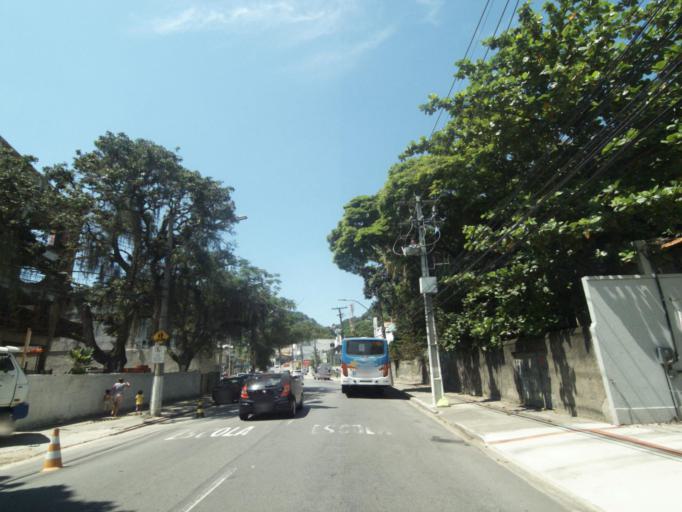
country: BR
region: Rio de Janeiro
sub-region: Niteroi
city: Niteroi
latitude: -22.9129
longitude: -43.0793
